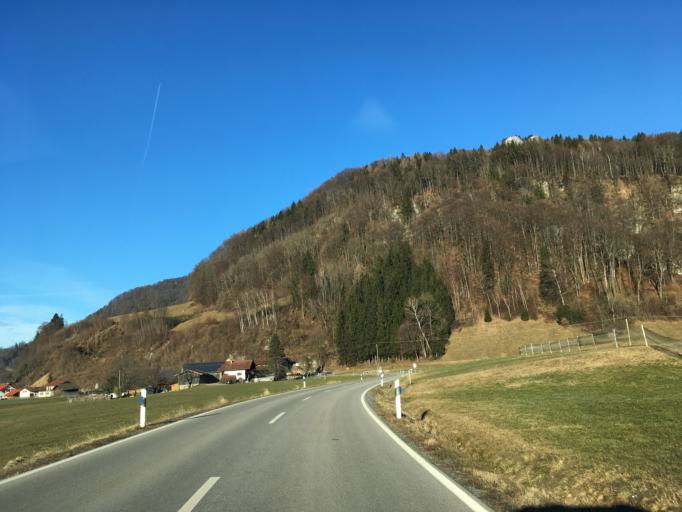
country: AT
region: Tyrol
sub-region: Politischer Bezirk Kufstein
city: Erl
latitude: 47.7079
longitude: 12.1639
